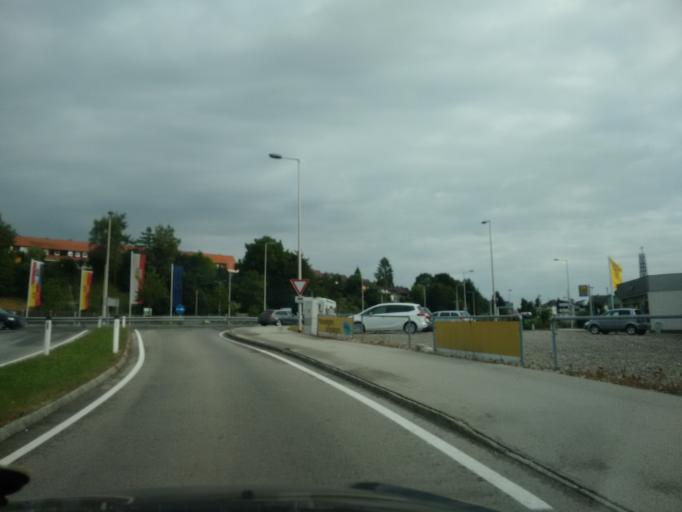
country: AT
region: Upper Austria
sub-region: Politischer Bezirk Vocklabruck
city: Lenzing
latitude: 47.9716
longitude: 13.6087
